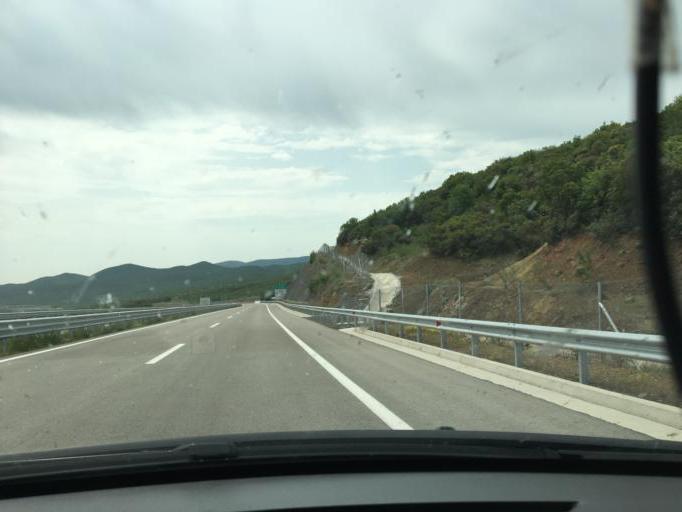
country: MK
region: Gevgelija
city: Miravci
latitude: 41.3047
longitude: 22.4274
